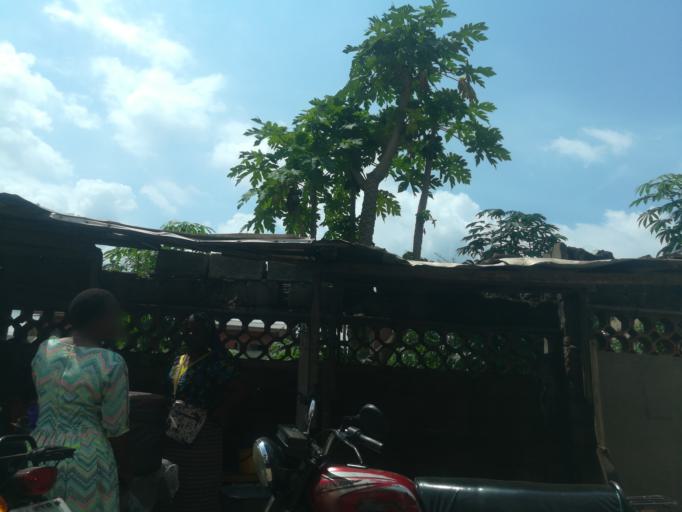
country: NG
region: Oyo
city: Ibadan
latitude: 7.3624
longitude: 3.8793
